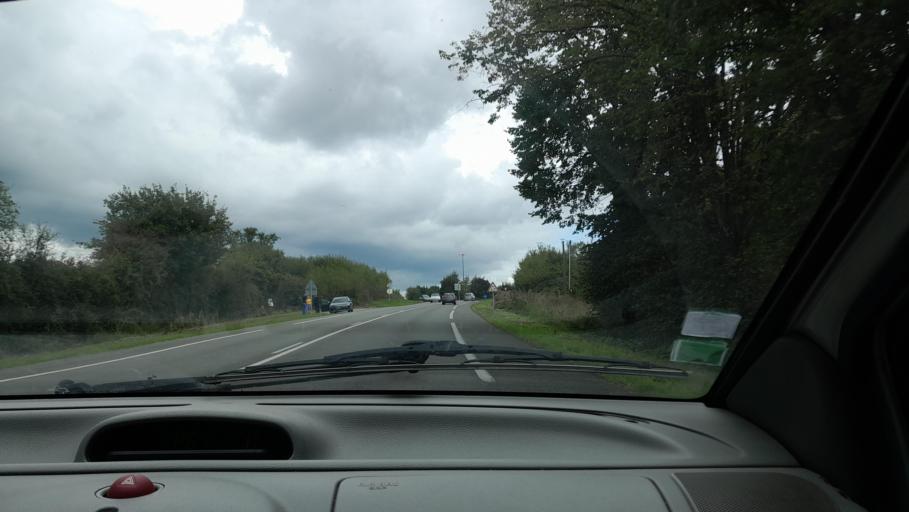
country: FR
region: Pays de la Loire
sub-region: Departement de la Mayenne
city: Montigne-le-Brillant
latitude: 48.0144
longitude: -0.8283
